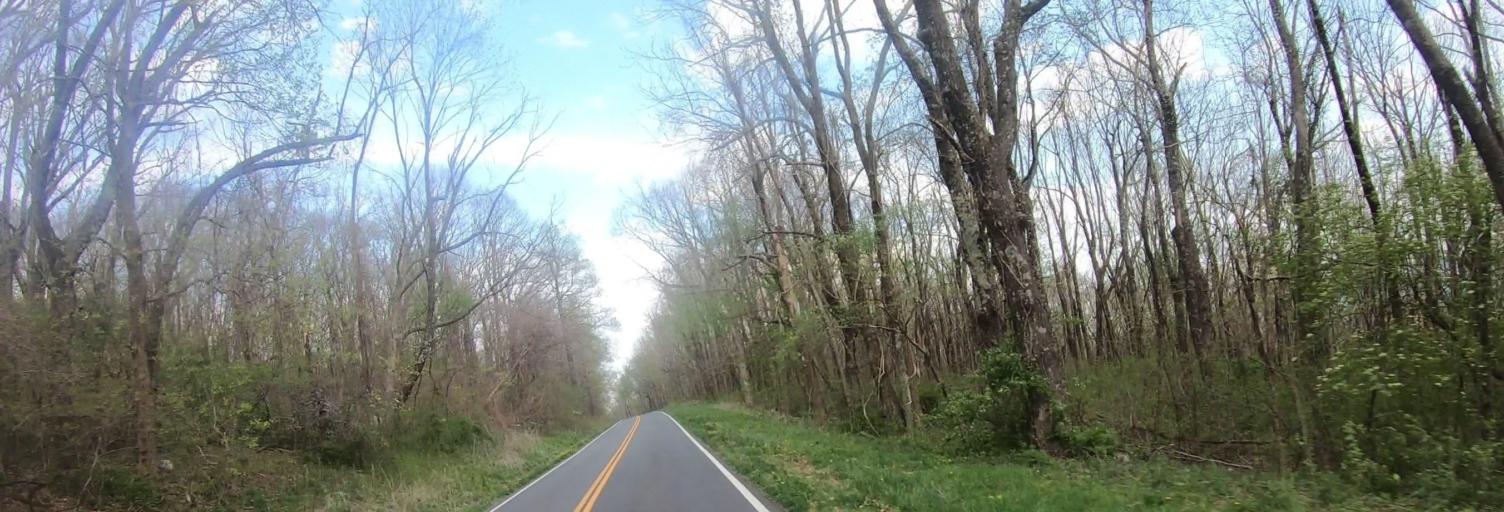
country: US
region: Virginia
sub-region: Augusta County
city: Dooms
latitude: 38.0633
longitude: -78.7999
